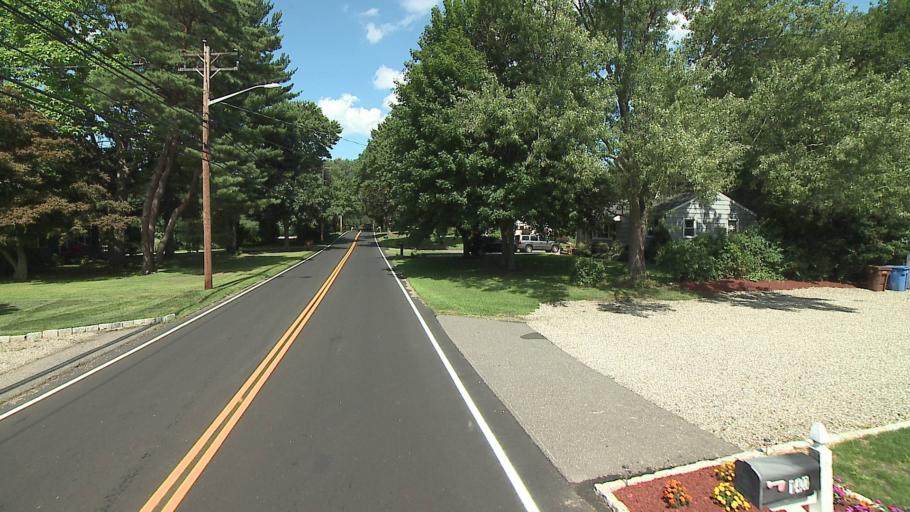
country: US
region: Connecticut
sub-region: Fairfield County
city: Trumbull
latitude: 41.2874
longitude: -73.1525
